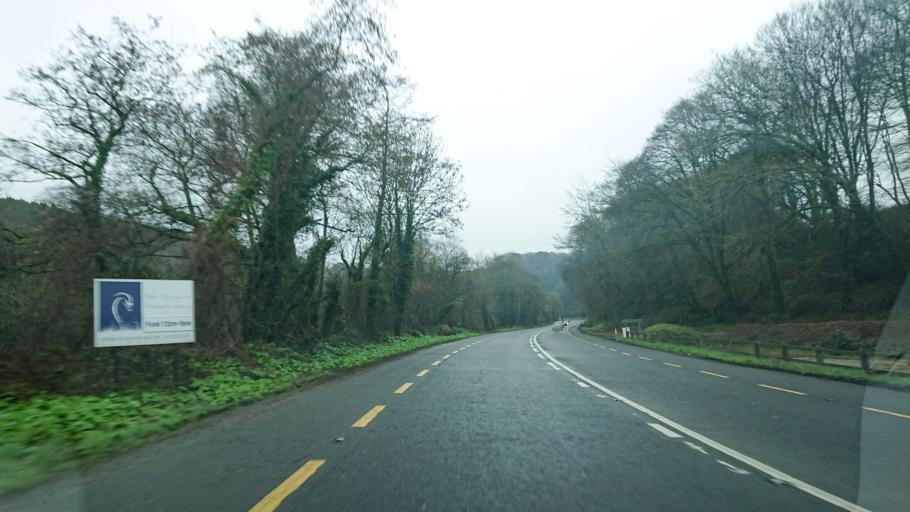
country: IE
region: Munster
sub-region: County Cork
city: Bandon
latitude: 51.7685
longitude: -8.6883
